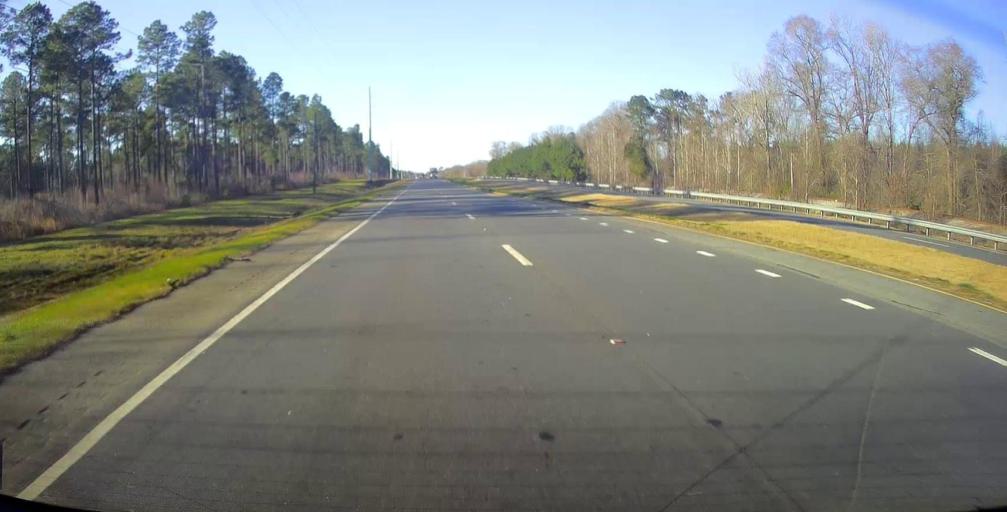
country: US
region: Georgia
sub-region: Lee County
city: Leesburg
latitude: 31.8689
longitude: -84.2371
